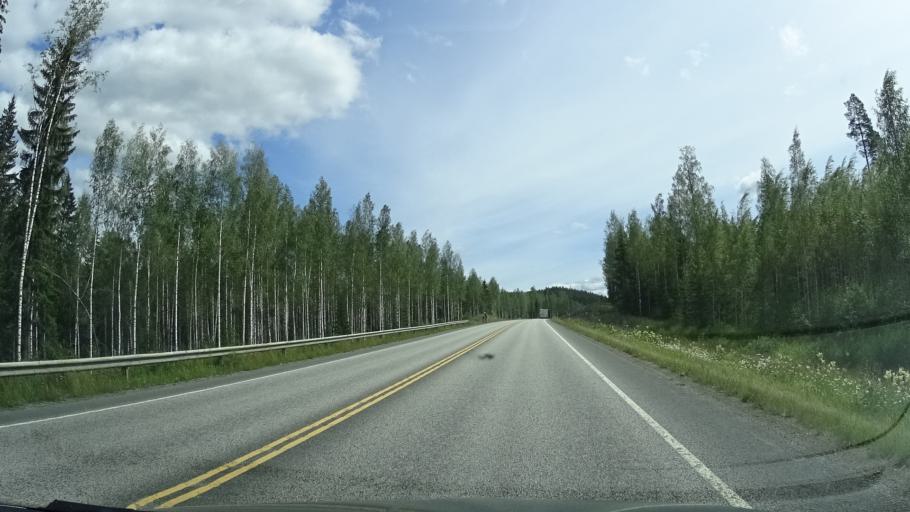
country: FI
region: Central Finland
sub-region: Jyvaeskylae
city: Jyvaeskylae
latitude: 62.2534
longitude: 25.6332
